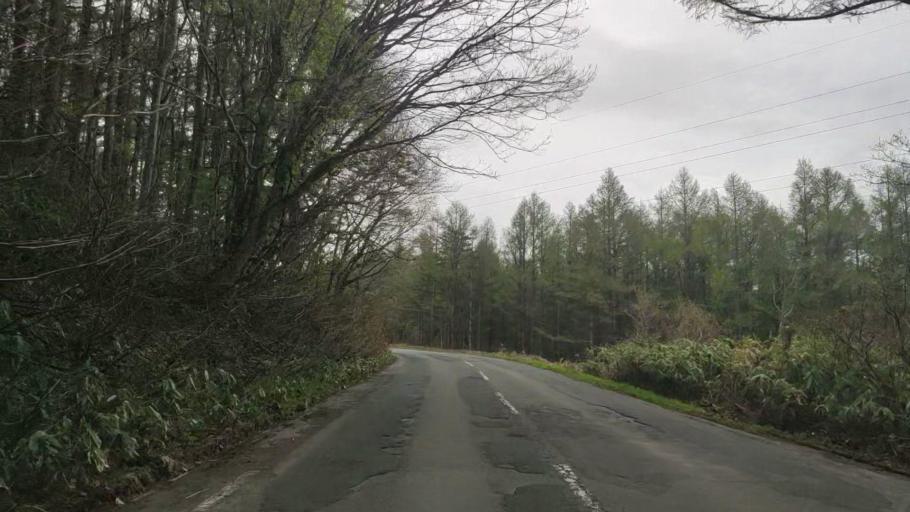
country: JP
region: Aomori
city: Aomori Shi
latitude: 40.7292
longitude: 140.8459
